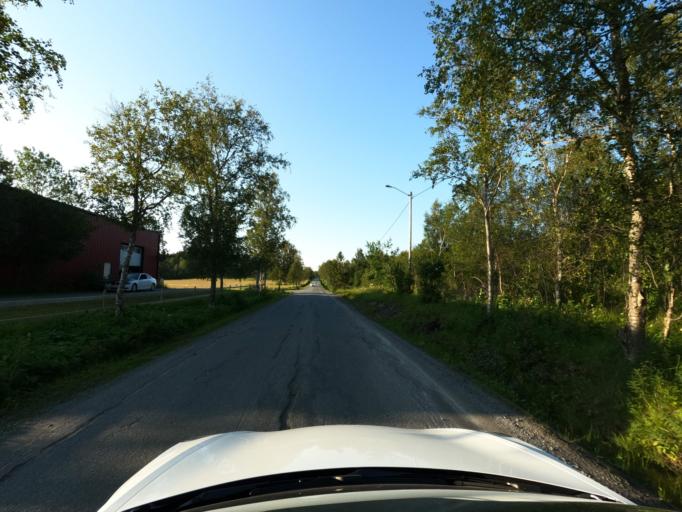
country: NO
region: Troms
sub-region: Skanland
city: Evenskjer
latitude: 68.4666
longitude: 16.7013
